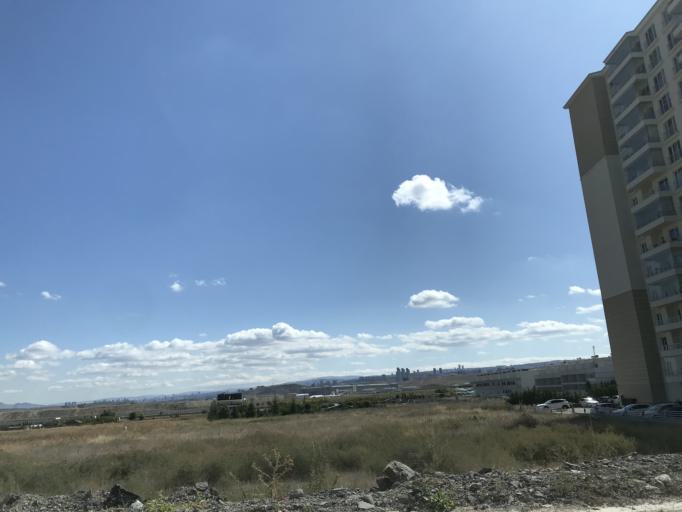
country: TR
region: Ankara
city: Etimesgut
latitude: 39.9141
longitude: 32.6456
